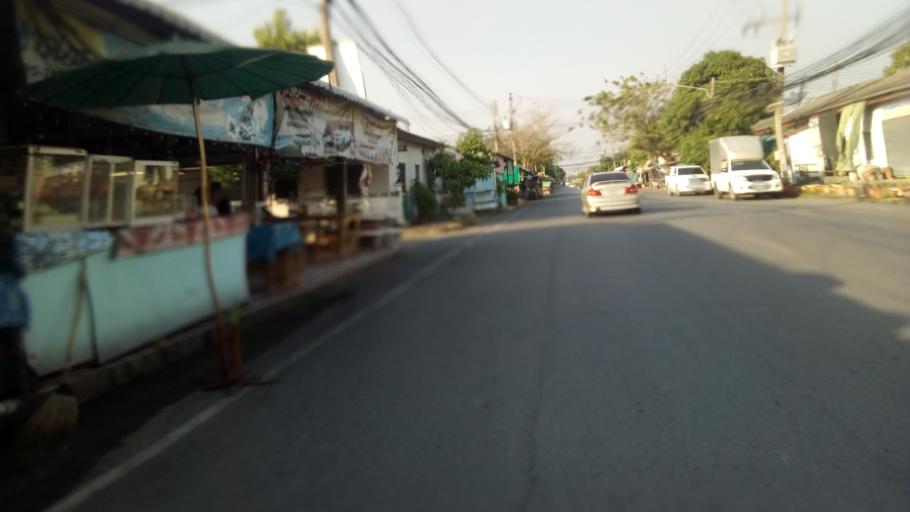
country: TH
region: Pathum Thani
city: Nong Suea
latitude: 14.0542
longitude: 100.8566
